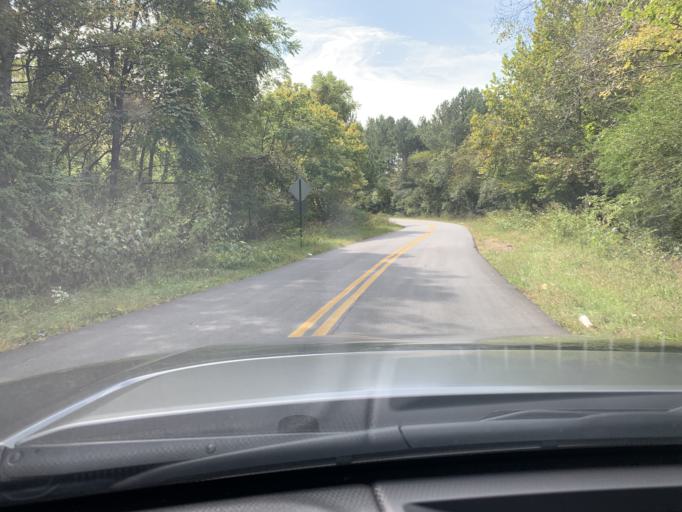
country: US
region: Georgia
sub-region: Polk County
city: Cedartown
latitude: 33.9562
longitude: -85.3514
